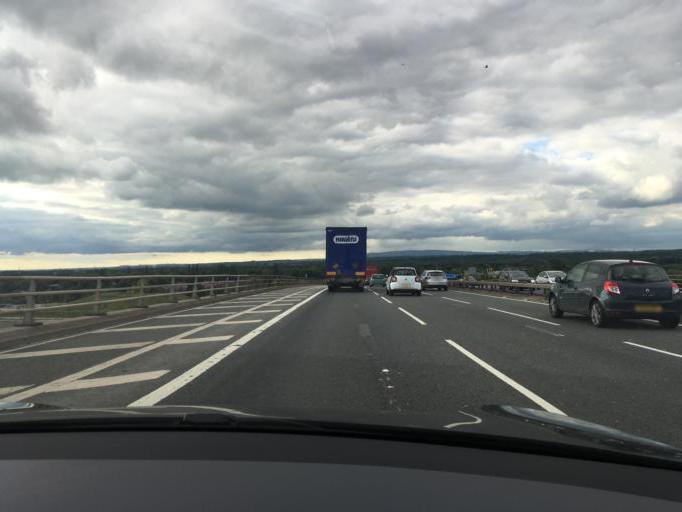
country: GB
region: England
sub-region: Trafford
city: Urmston
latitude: 53.4696
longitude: -2.3695
